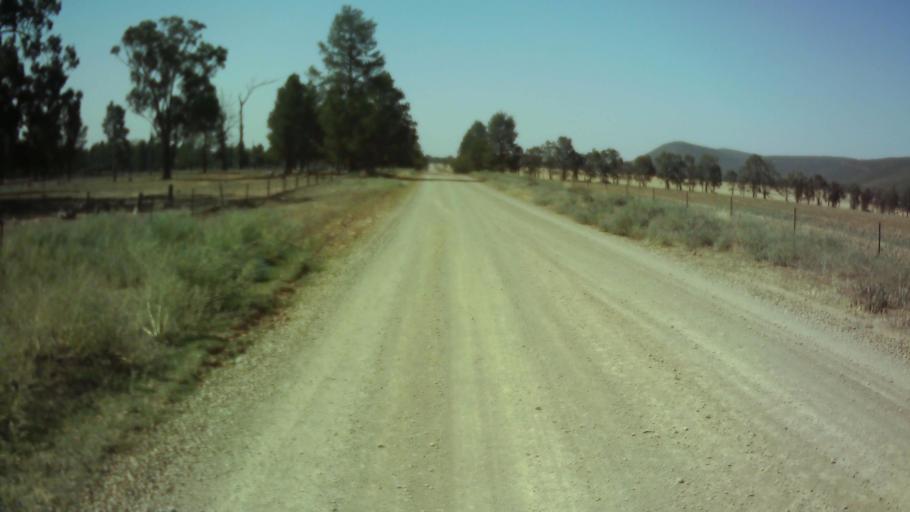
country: AU
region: New South Wales
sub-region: Weddin
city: Grenfell
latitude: -33.9377
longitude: 147.9293
